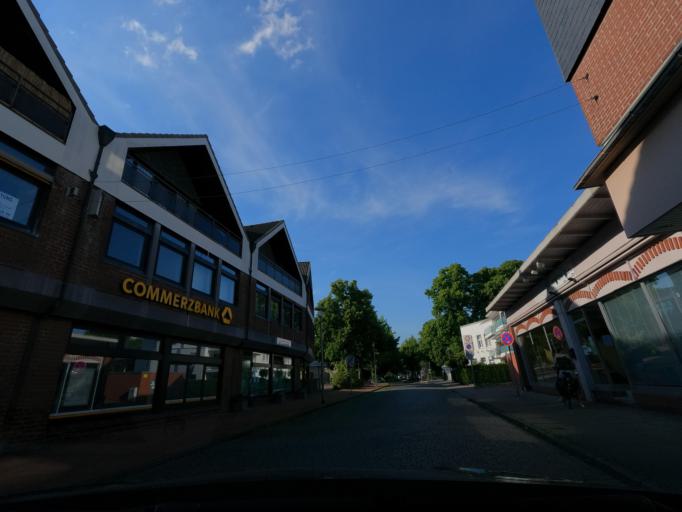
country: DE
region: Schleswig-Holstein
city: Uetersen
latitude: 53.6825
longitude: 9.6674
